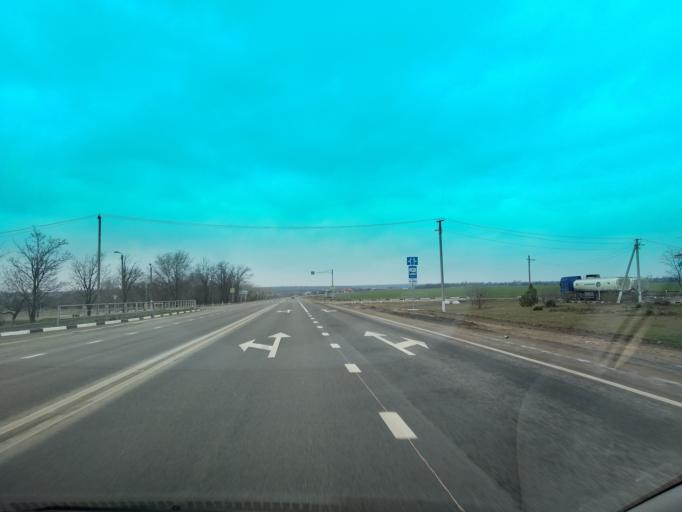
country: RU
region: Krasnodarskiy
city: Novomalorossiyskaya
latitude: 45.7076
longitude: 39.8475
